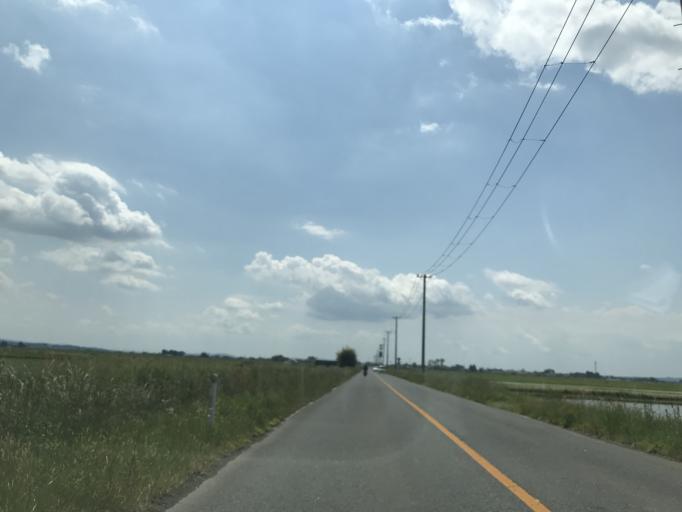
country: JP
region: Miyagi
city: Kogota
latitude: 38.5943
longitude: 141.0271
